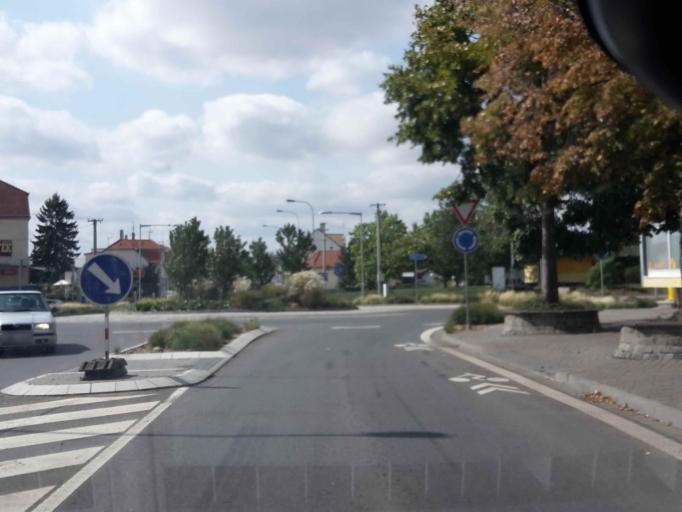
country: CZ
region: South Moravian
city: Rousinov
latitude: 49.2030
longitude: 16.8799
